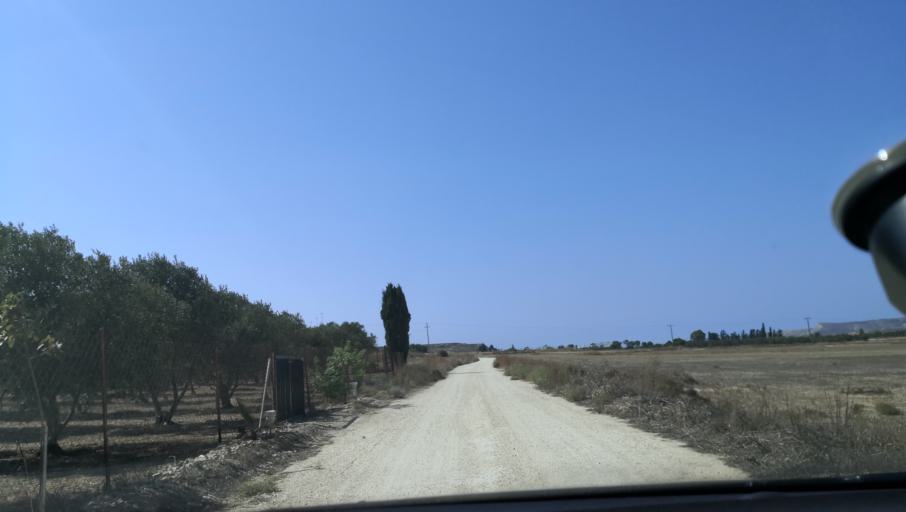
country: CY
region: Lefkosia
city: Mammari
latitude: 35.1770
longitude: 33.2158
